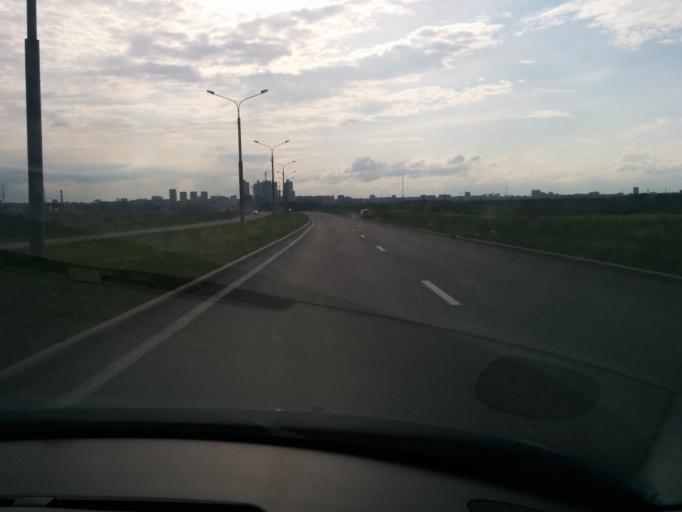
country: RU
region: Perm
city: Perm
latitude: 58.0065
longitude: 56.3557
